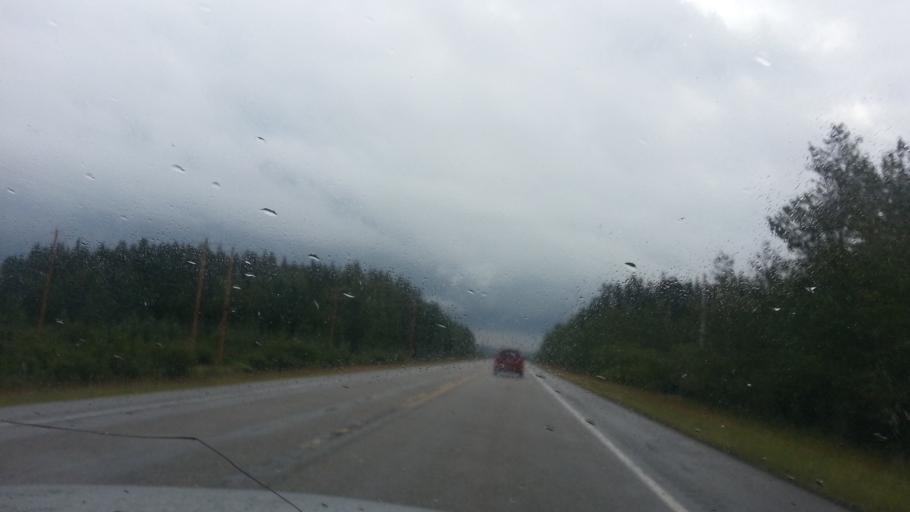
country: CA
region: Alberta
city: Cochrane
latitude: 50.9214
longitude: -114.5959
